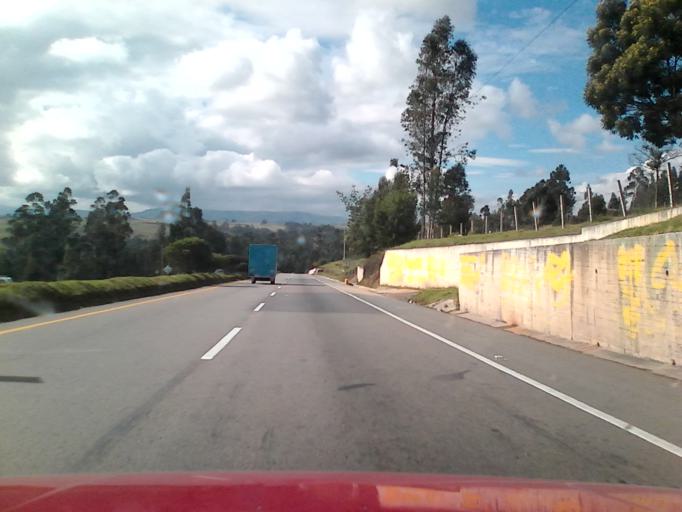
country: CO
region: Boyaca
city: Tuta
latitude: 5.6693
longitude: -73.2699
